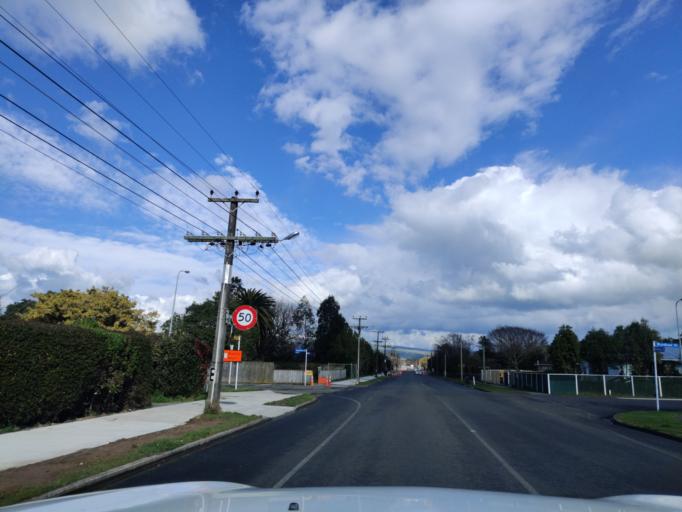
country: NZ
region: Manawatu-Wanganui
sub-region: Palmerston North City
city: Palmerston North
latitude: -40.2835
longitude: 175.7600
